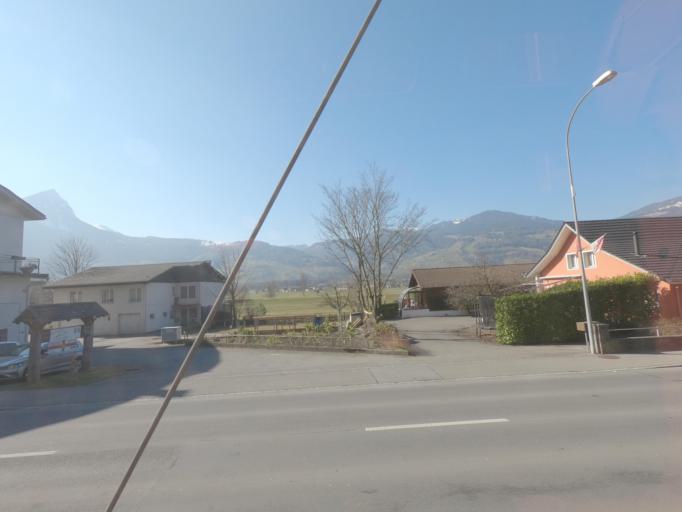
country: CH
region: Obwalden
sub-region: Obwalden
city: Giswil
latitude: 46.8353
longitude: 8.1855
